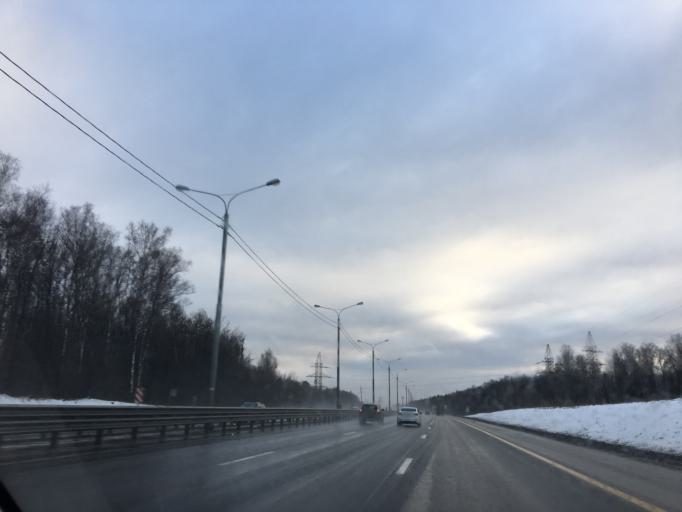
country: RU
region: Moskovskaya
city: L'vovskiy
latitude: 55.3050
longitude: 37.5491
